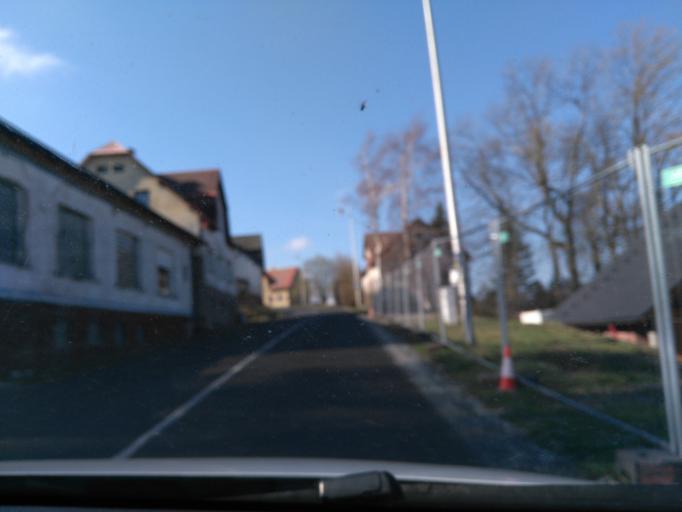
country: CZ
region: Ustecky
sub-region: Okres Chomutov
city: Vejprty
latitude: 50.4922
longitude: 13.0377
